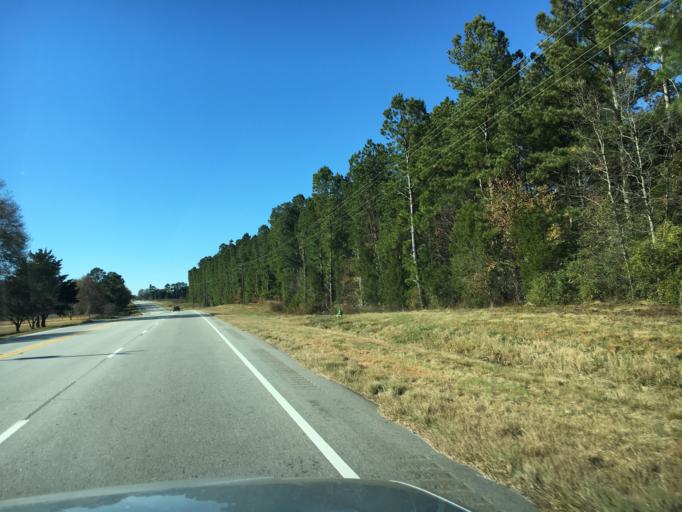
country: US
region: Georgia
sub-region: Hart County
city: Royston
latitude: 34.2932
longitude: -83.0277
